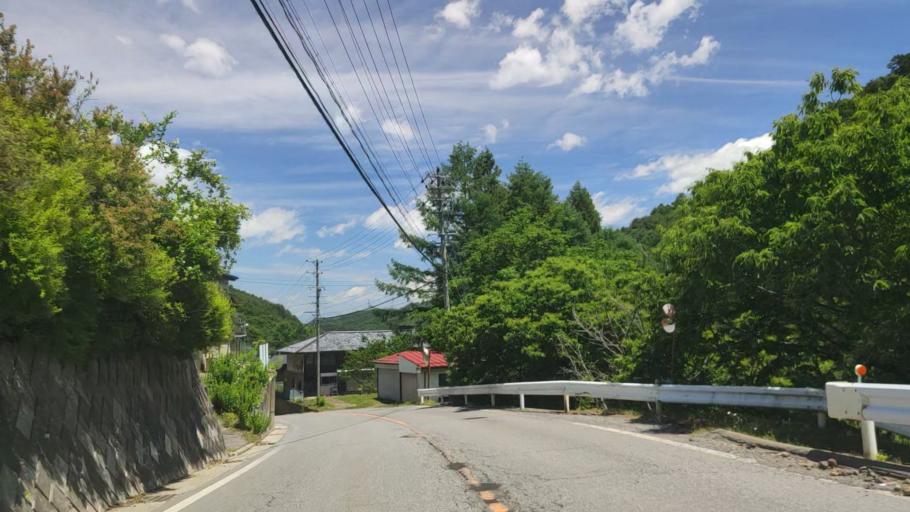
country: JP
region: Nagano
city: Kamimaruko
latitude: 36.1719
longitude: 138.2410
